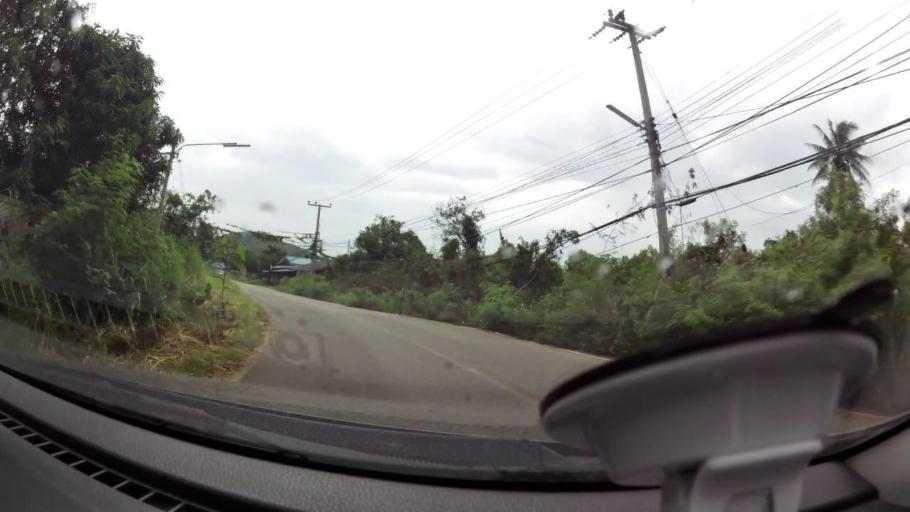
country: TH
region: Prachuap Khiri Khan
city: Pran Buri
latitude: 12.4443
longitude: 99.9691
